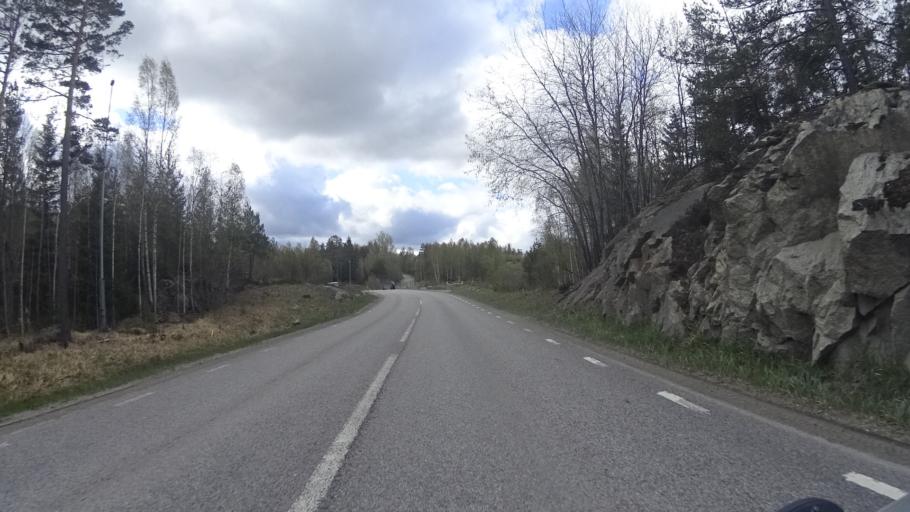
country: SE
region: Stockholm
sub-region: Botkyrka Kommun
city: Tullinge
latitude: 59.1858
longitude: 17.9280
